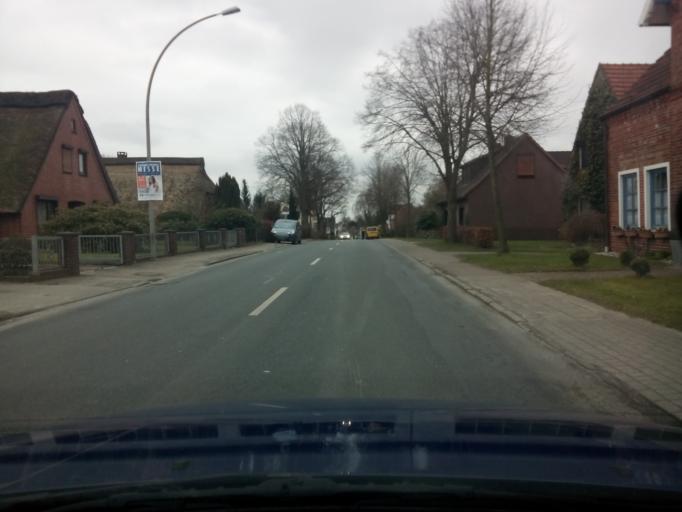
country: DE
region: Lower Saxony
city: Osterholz-Scharmbeck
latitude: 53.2307
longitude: 8.8097
